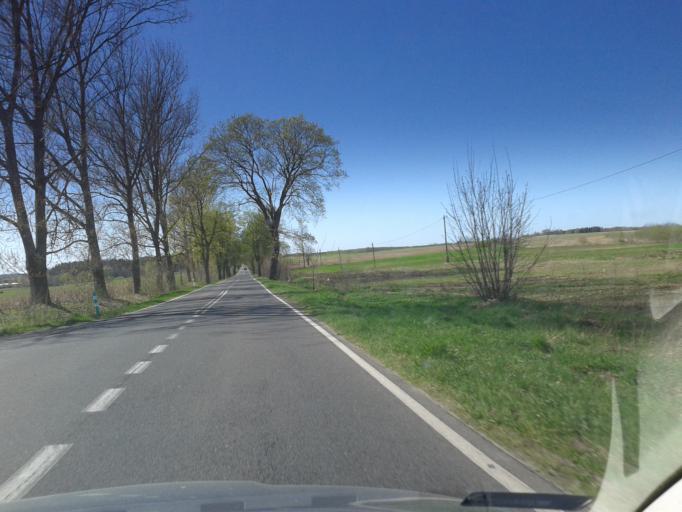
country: PL
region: West Pomeranian Voivodeship
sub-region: Powiat szczecinecki
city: Barwice
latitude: 53.7204
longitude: 16.4131
